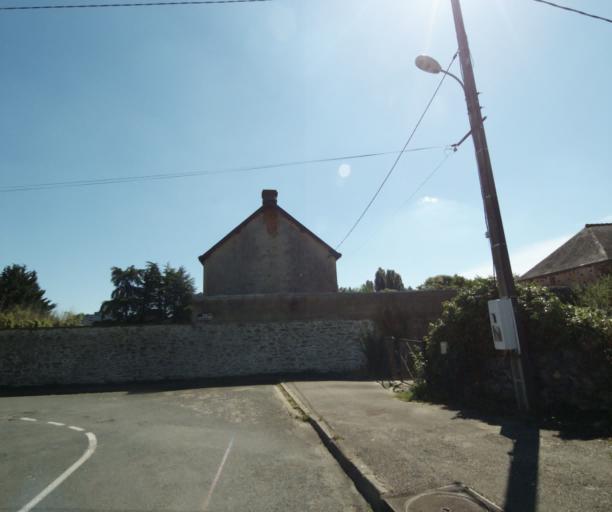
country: FR
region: Pays de la Loire
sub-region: Departement de la Mayenne
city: Laval
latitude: 48.0656
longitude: -0.7541
